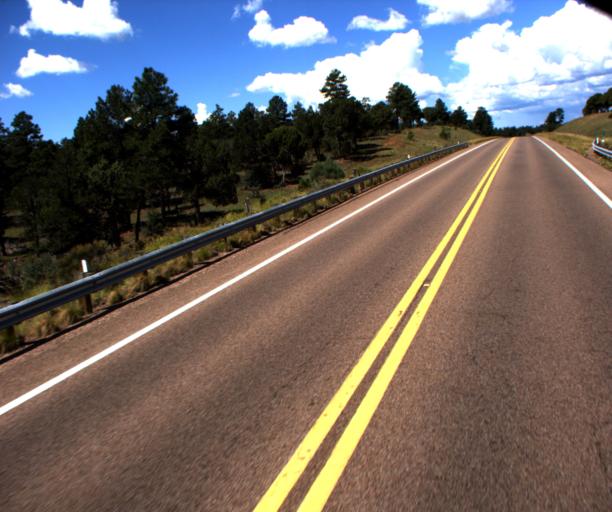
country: US
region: Arizona
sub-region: Navajo County
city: Heber-Overgaard
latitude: 34.3675
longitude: -110.3777
